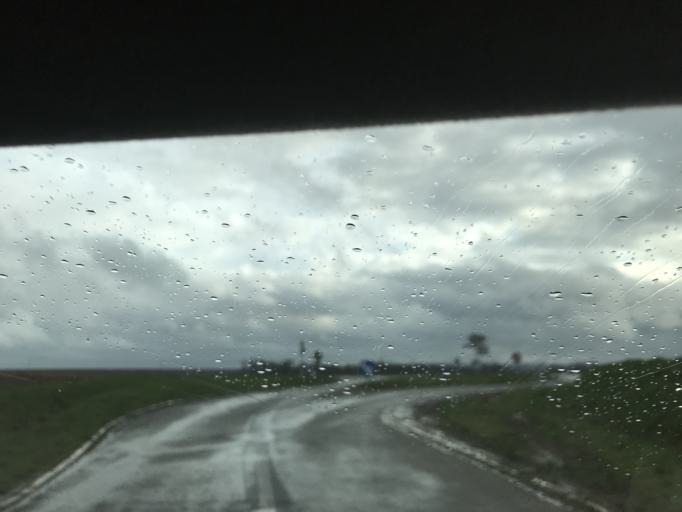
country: FR
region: Picardie
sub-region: Departement de l'Aisne
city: Billy-sur-Aisne
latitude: 49.3429
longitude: 3.3810
